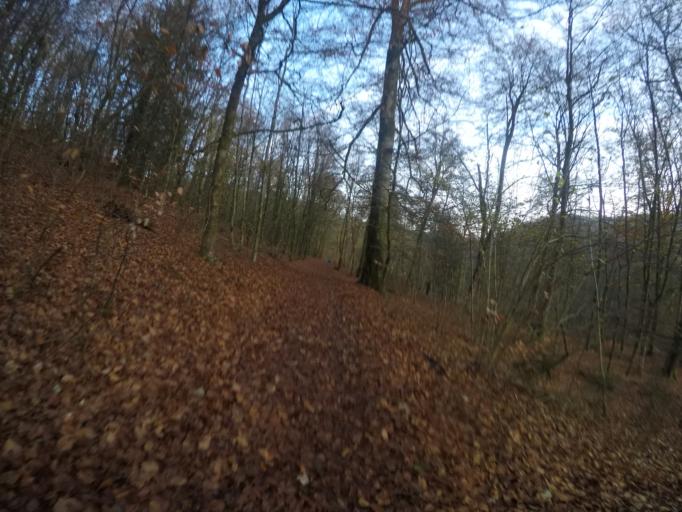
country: BE
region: Wallonia
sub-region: Province du Luxembourg
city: Habay-la-Vieille
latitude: 49.7377
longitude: 5.6689
